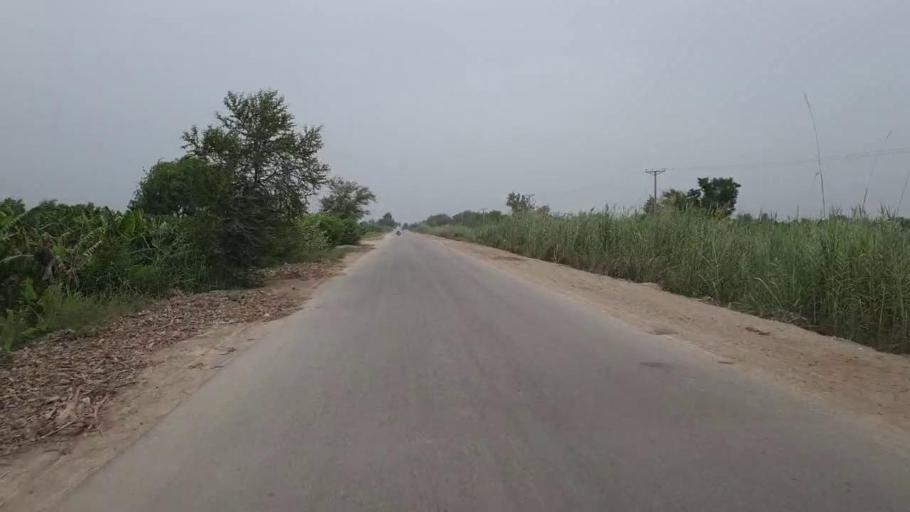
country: PK
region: Sindh
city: Bandhi
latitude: 26.5490
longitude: 68.2157
